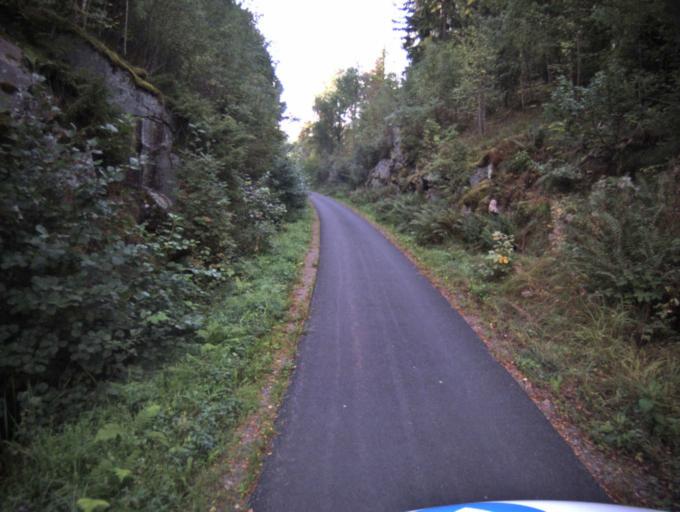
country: SE
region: Vaestra Goetaland
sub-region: Ulricehamns Kommun
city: Ulricehamn
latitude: 57.7610
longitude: 13.3990
